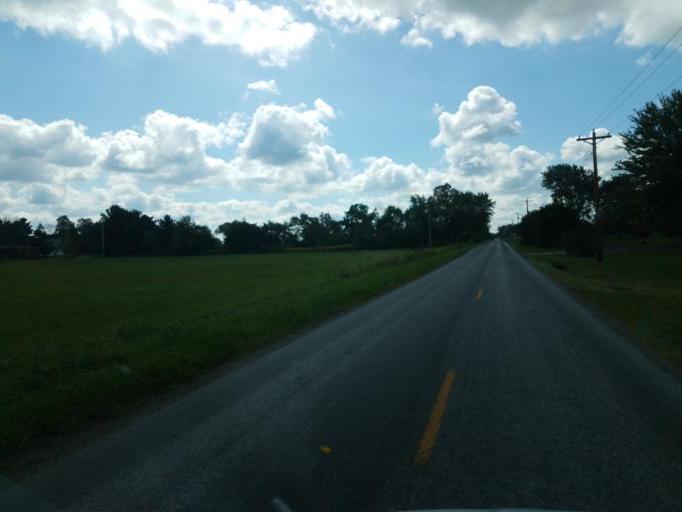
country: US
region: Ohio
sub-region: Wayne County
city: West Salem
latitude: 41.0246
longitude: -82.1264
